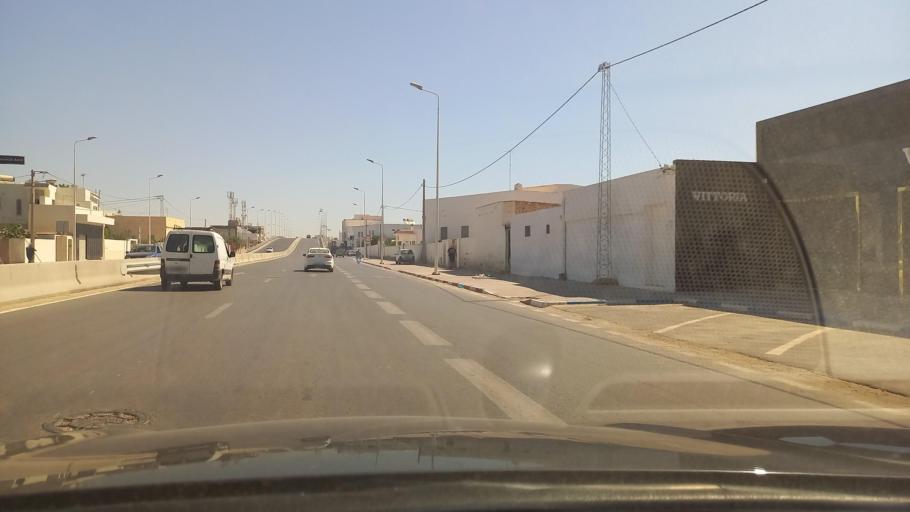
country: TN
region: Safaqis
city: Sfax
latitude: 34.7541
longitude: 10.7325
